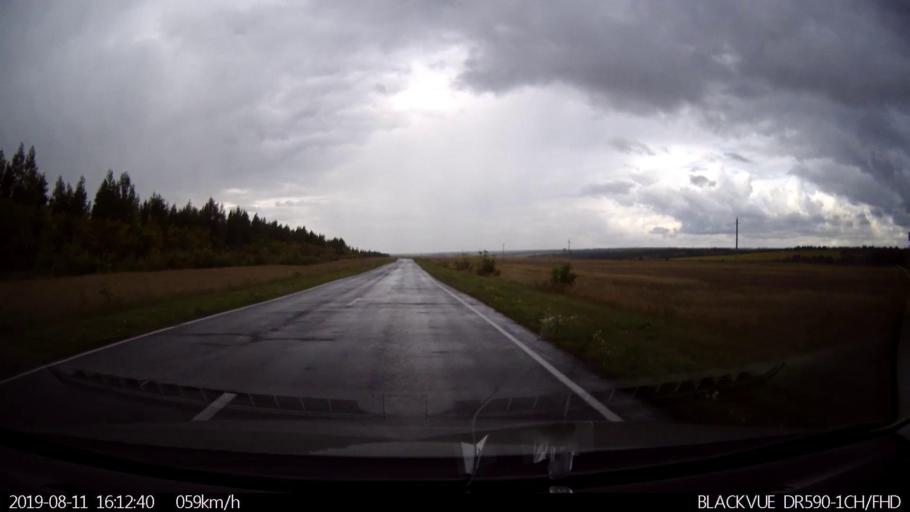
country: RU
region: Ulyanovsk
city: Ignatovka
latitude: 54.0134
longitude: 47.6397
